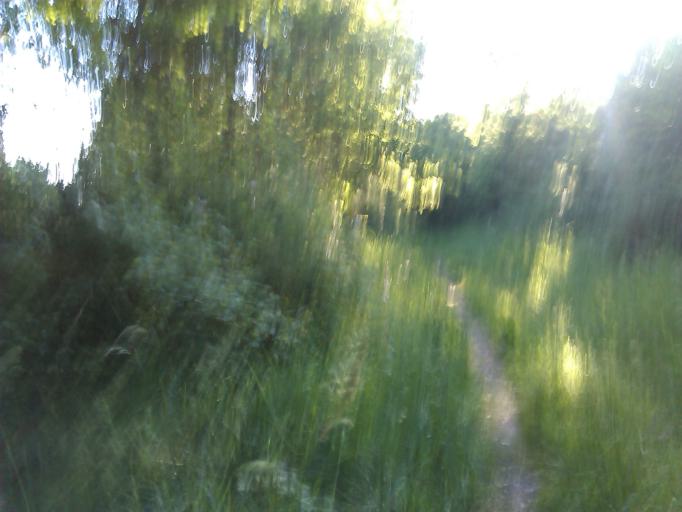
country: FR
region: Centre
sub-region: Departement de l'Indre
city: Le Blanc
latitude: 46.6005
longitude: 1.0112
